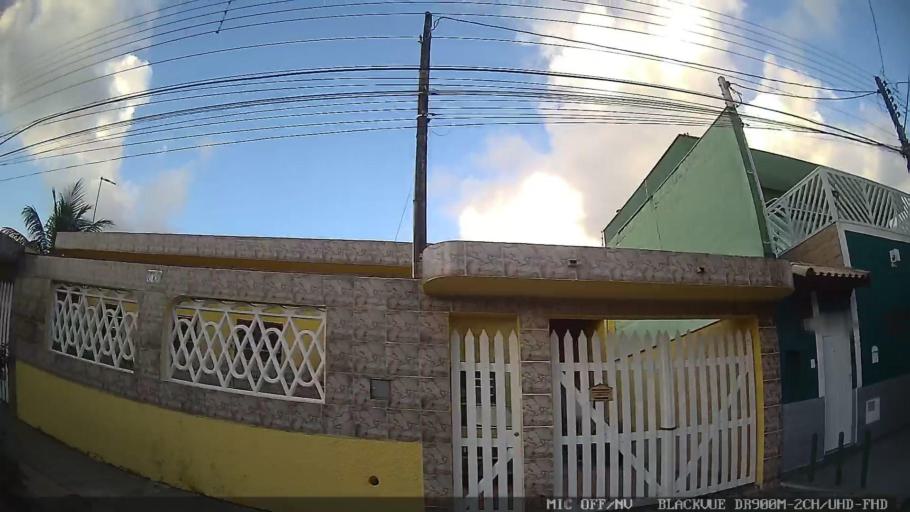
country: BR
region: Sao Paulo
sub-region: Itanhaem
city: Itanhaem
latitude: -24.1449
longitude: -46.7258
